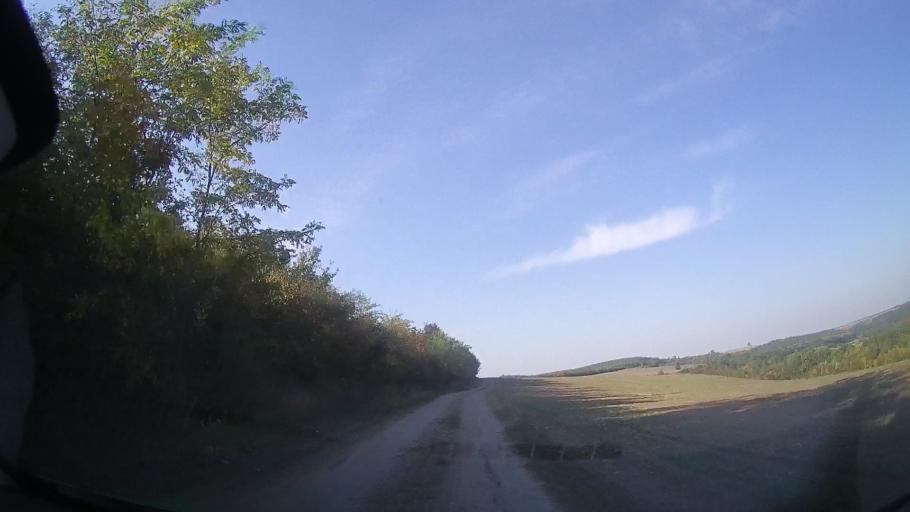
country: RO
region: Timis
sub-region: Comuna Bogda
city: Bogda
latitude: 45.9128
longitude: 21.6053
